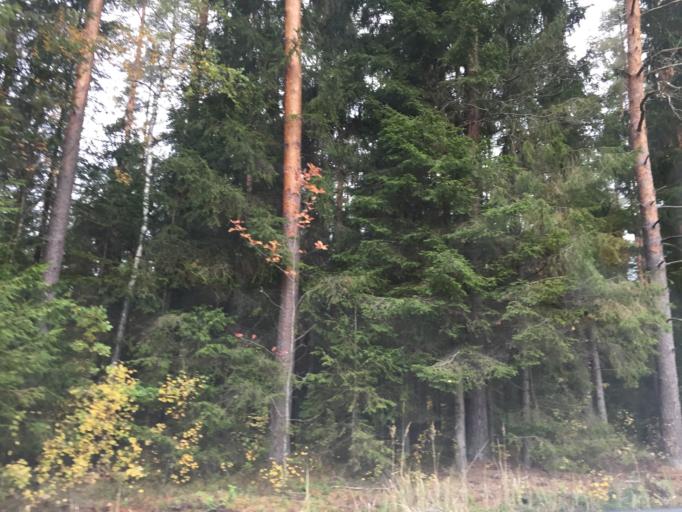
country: LV
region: Jelgava
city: Jelgava
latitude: 56.7318
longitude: 23.6902
